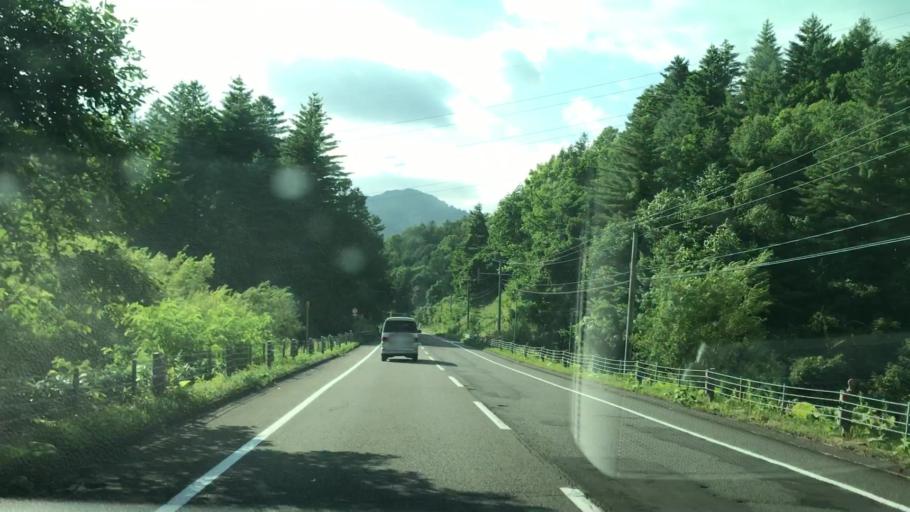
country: JP
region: Hokkaido
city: Shimo-furano
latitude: 42.8893
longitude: 142.1983
